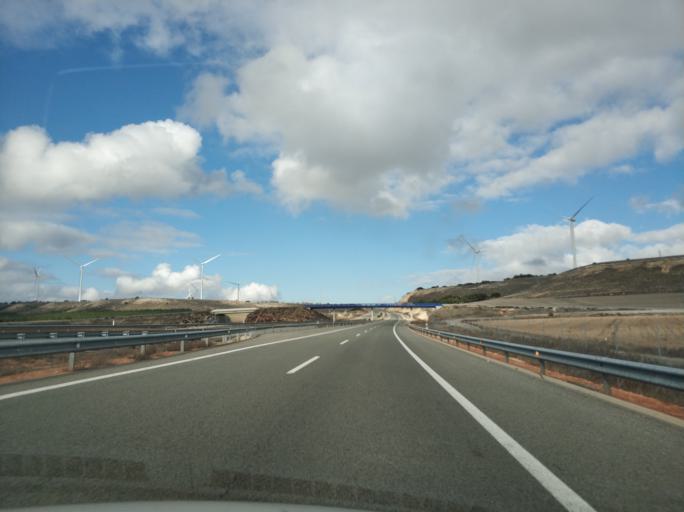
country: ES
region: Castille and Leon
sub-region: Provincia de Soria
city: Alcubilla de las Penas
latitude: 41.2829
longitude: -2.4758
